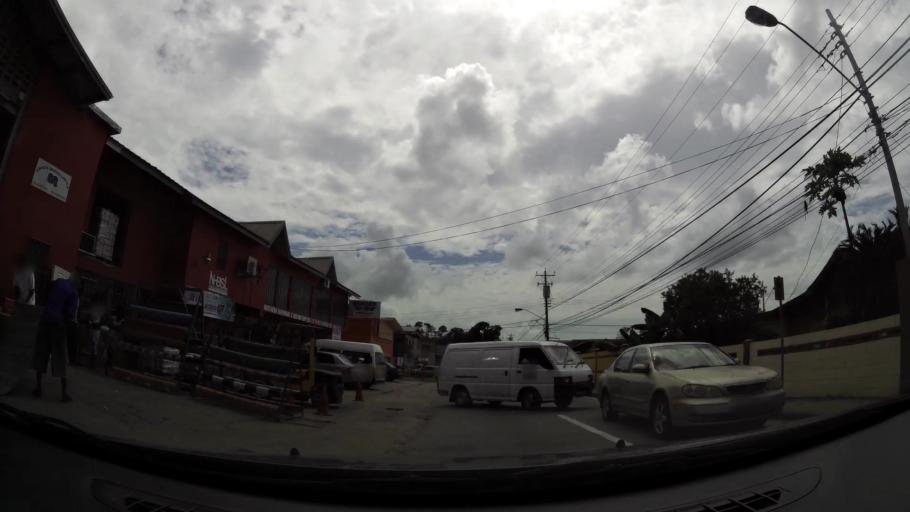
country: TT
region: Diego Martin
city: Petit Valley
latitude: 10.6913
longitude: -61.5545
